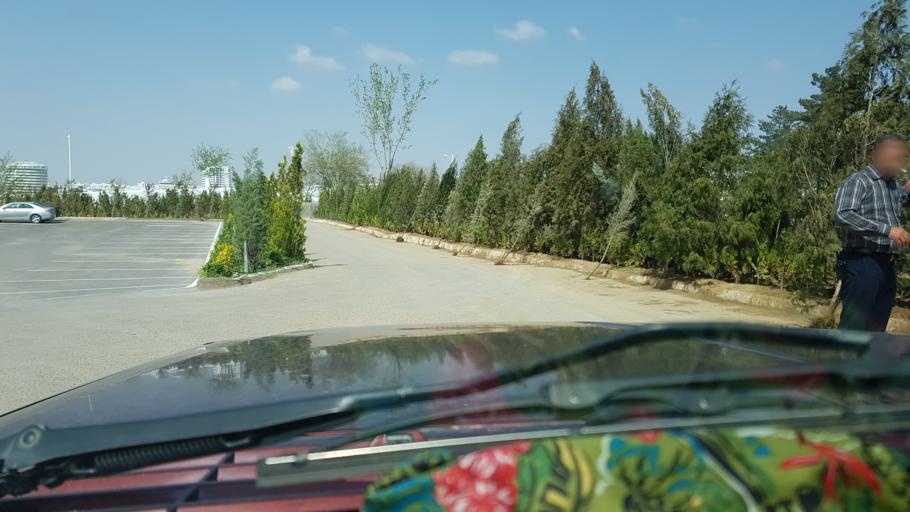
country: TM
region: Ahal
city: Ashgabat
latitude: 37.8809
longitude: 58.3708
